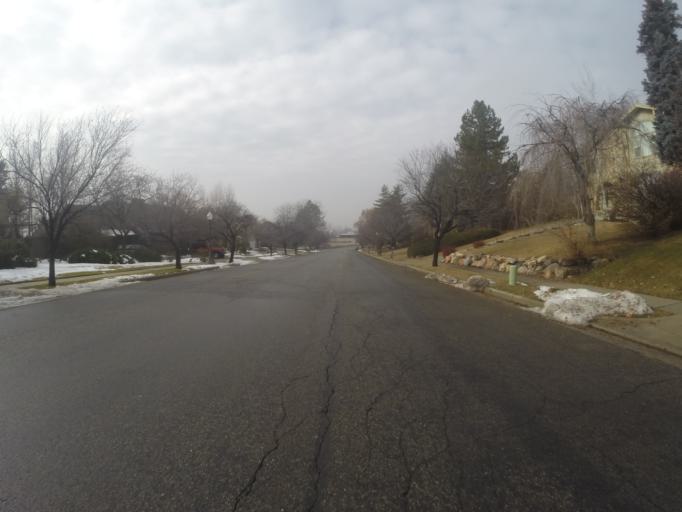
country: US
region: Utah
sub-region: Salt Lake County
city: Salt Lake City
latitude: 40.7748
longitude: -111.8503
